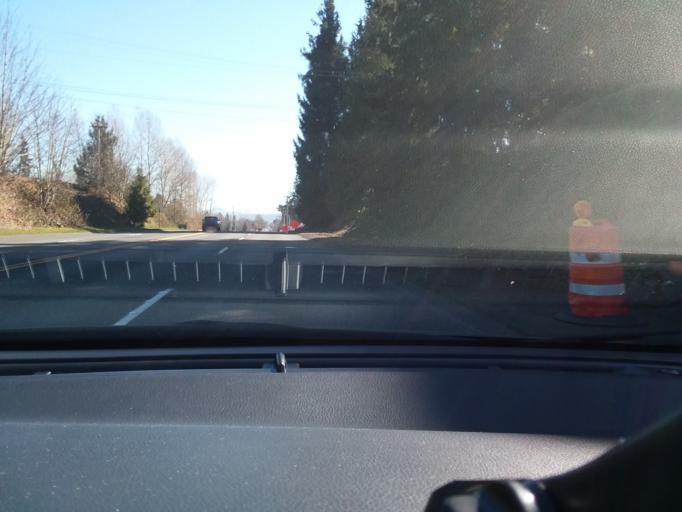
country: US
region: Washington
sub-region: Pierce County
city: Puyallup
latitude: 47.1902
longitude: -122.3305
